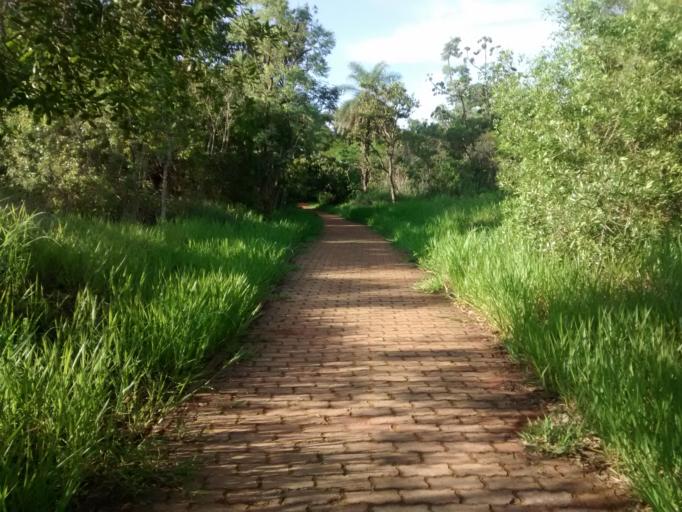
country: BR
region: Federal District
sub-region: Brasilia
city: Brasilia
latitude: -15.7438
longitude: -47.8853
